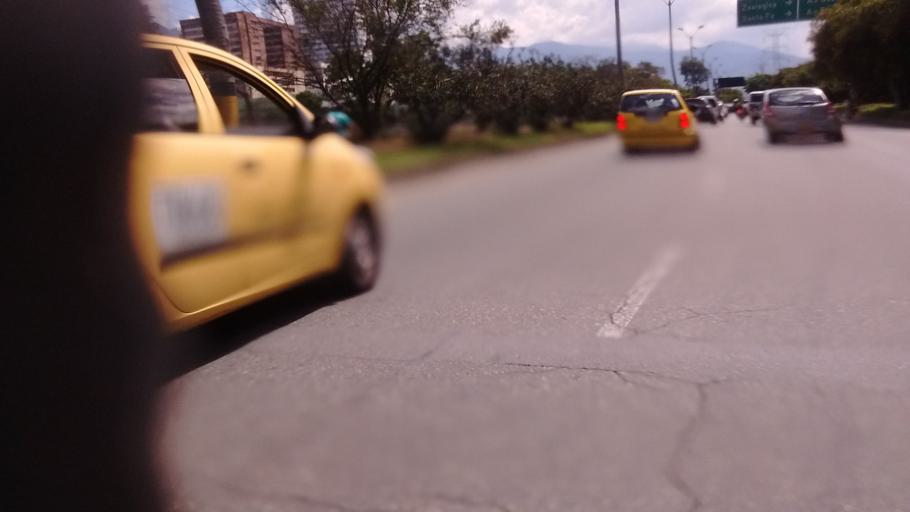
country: CO
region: Antioquia
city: Medellin
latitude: 6.2269
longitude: -75.5766
